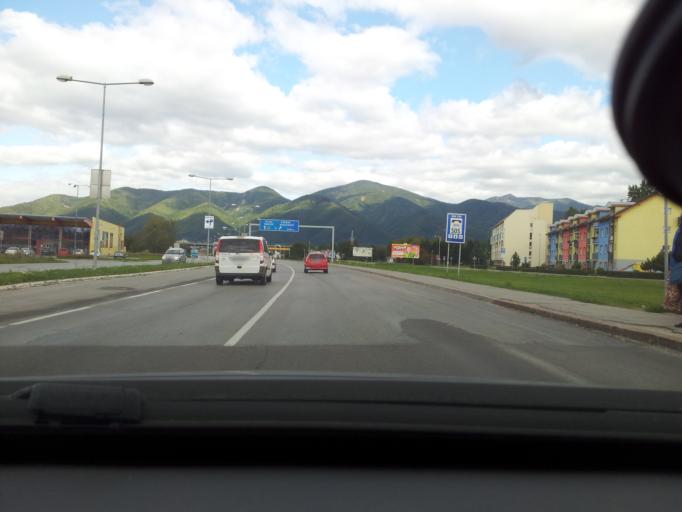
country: SK
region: Zilinsky
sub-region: Okres Martin
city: Martin
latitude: 49.0892
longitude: 18.9332
